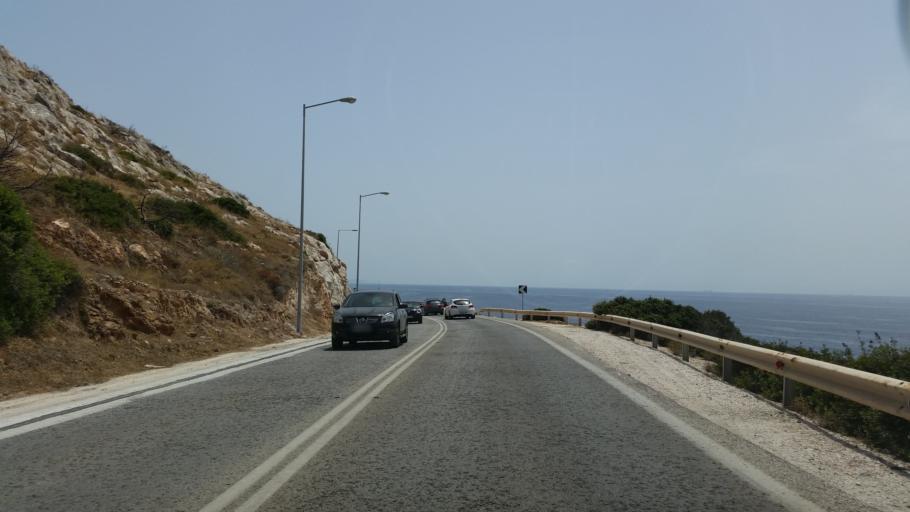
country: GR
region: Attica
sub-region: Nomarchia Anatolikis Attikis
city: Palaia Fokaia
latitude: 37.7084
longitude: 23.9363
